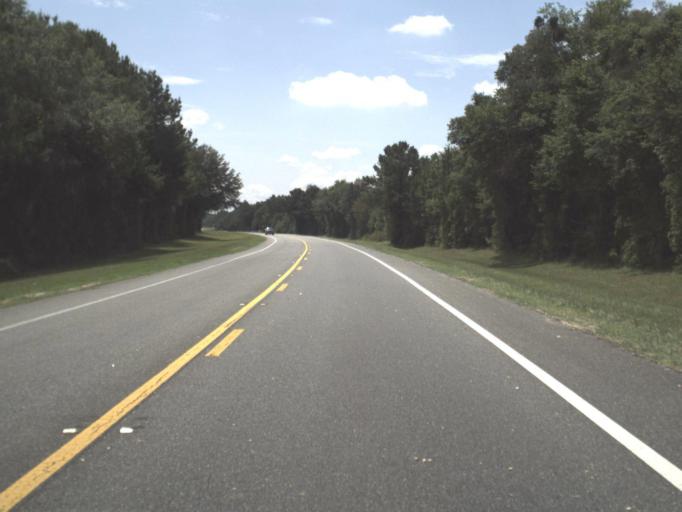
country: US
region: Florida
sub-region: Suwannee County
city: Live Oak
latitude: 30.1779
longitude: -82.9841
